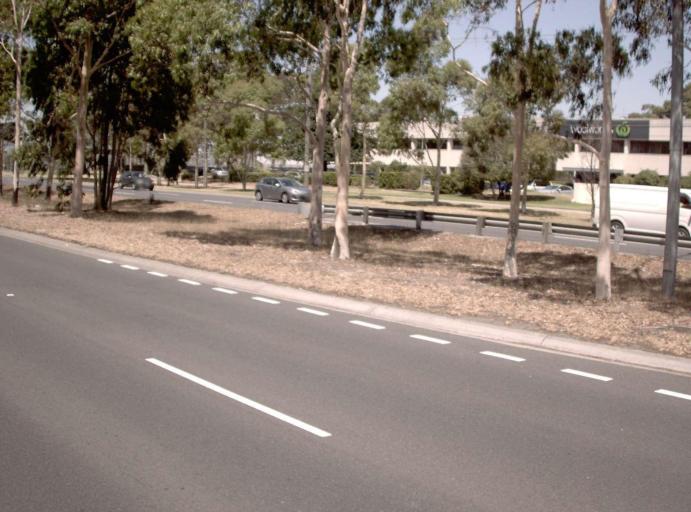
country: AU
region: Victoria
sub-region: Monash
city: Mulgrave
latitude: -37.9215
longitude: 145.1834
